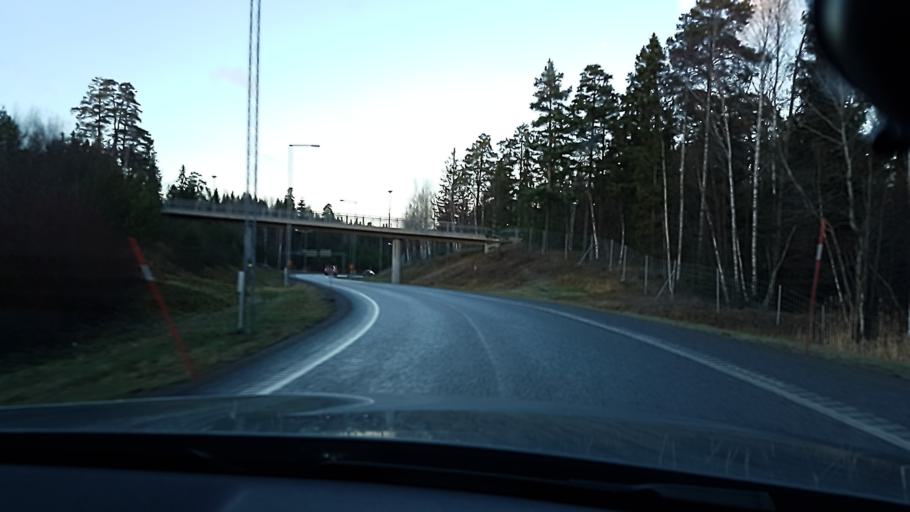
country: SE
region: Stockholm
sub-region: Sodertalje Kommun
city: Pershagen
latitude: 59.1589
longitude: 17.6493
